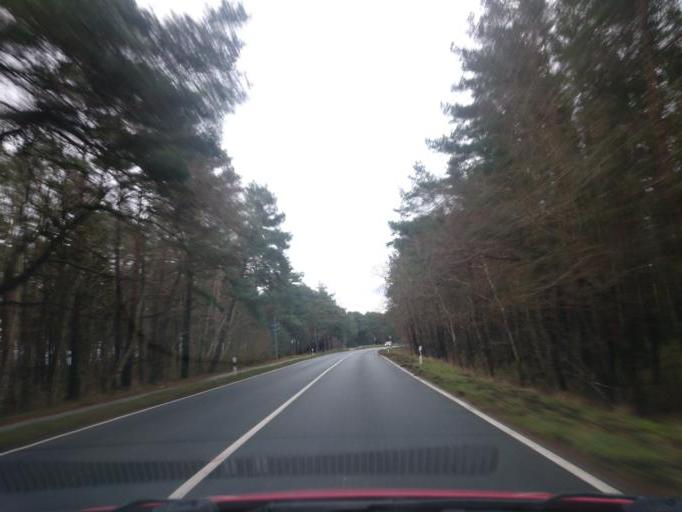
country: DE
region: Mecklenburg-Vorpommern
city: Glowe
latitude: 54.5702
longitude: 13.4456
